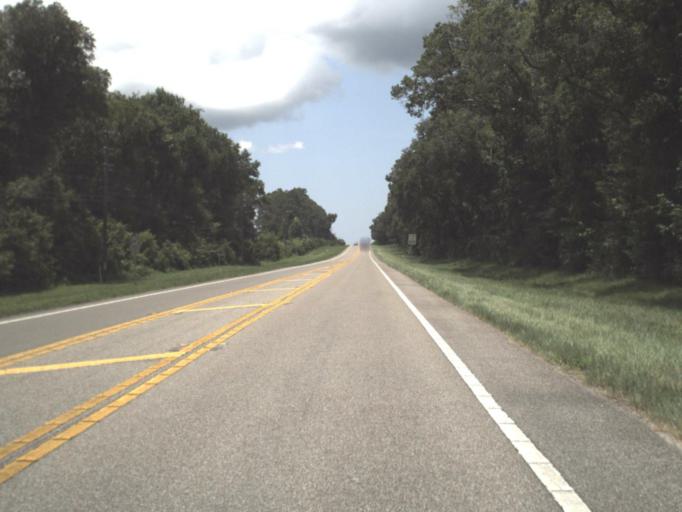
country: US
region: Florida
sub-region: Hernando County
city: North Brooksville
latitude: 28.6526
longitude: -82.4493
